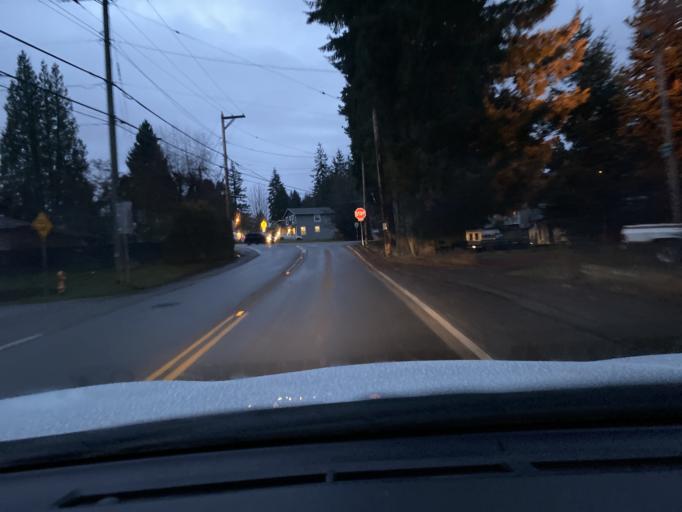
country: US
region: Washington
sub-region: Snohomish County
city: Martha Lake
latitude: 47.8704
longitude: -122.2597
